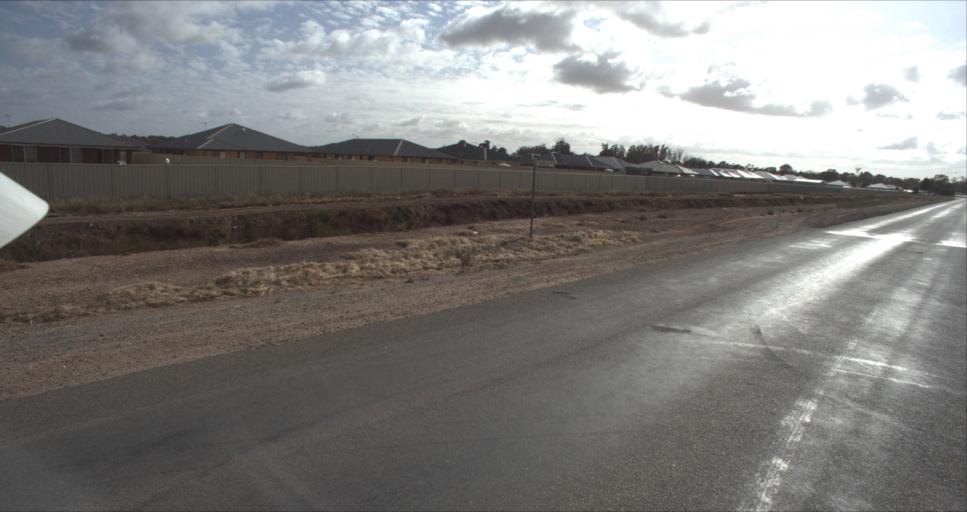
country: AU
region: New South Wales
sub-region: Leeton
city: Leeton
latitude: -34.5713
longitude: 146.3989
